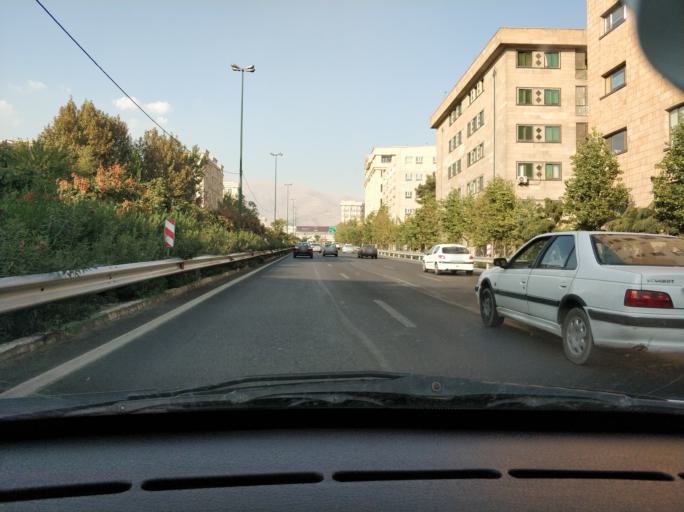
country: IR
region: Tehran
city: Tajrish
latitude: 35.7661
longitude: 51.4679
